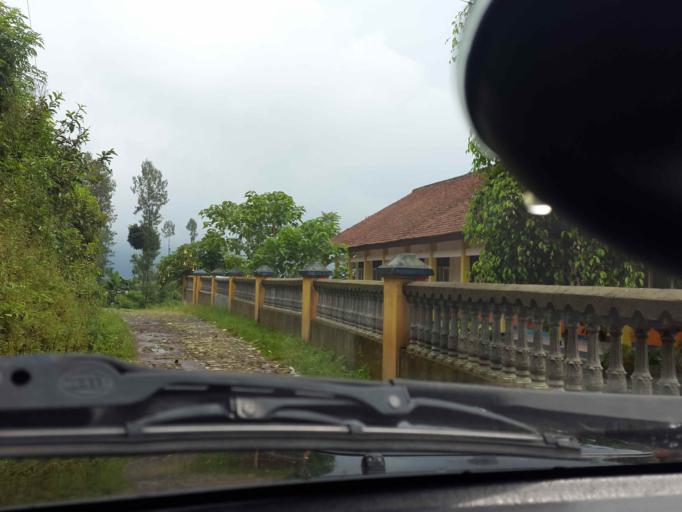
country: ID
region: Central Java
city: Wonosobo
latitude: -7.3906
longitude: 110.0122
